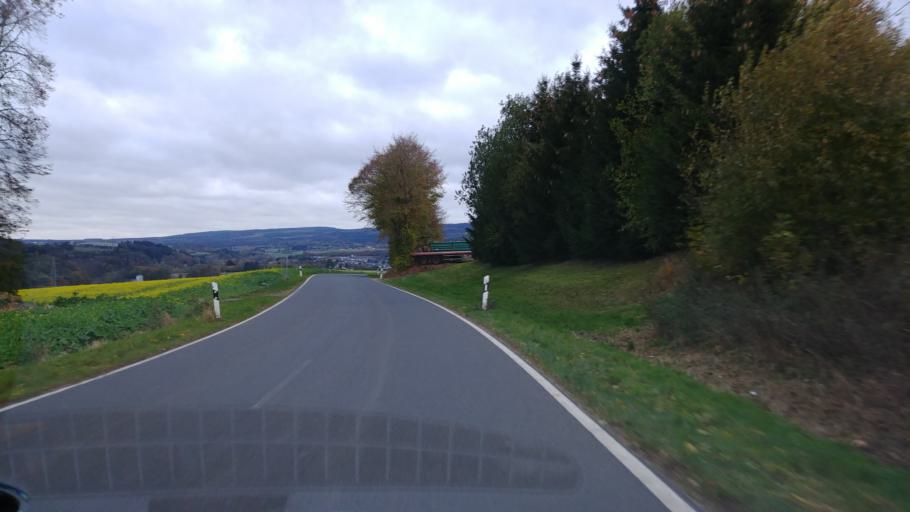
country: DE
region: Rheinland-Pfalz
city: Morbach
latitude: 49.8077
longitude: 7.0990
